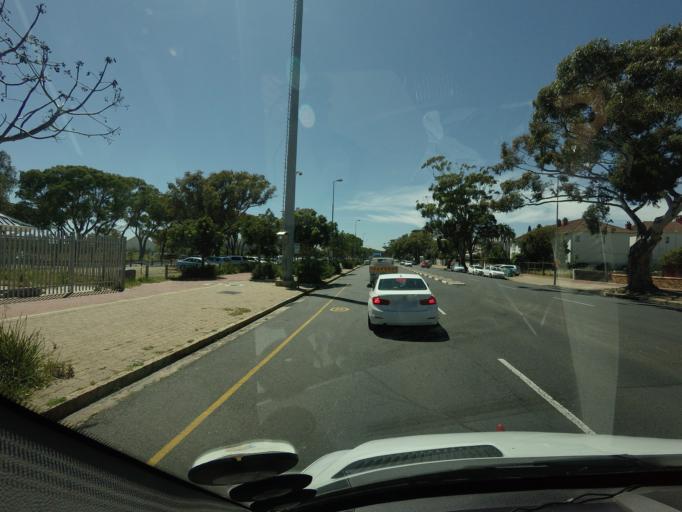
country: ZA
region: Western Cape
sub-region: City of Cape Town
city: Cape Town
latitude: -33.9076
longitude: 18.4057
